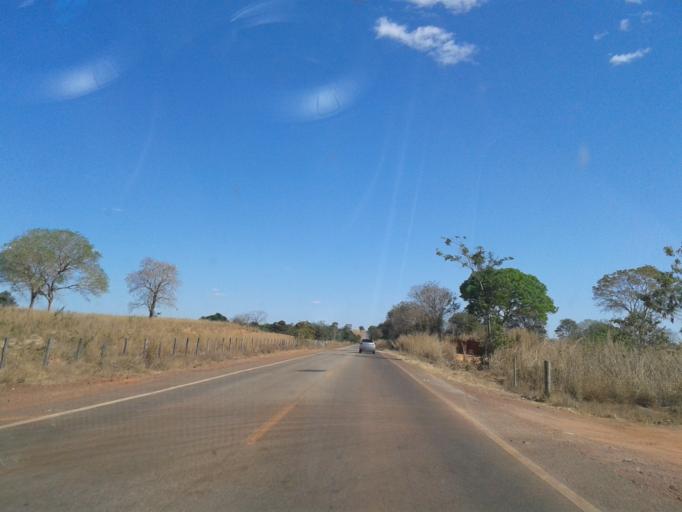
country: BR
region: Goias
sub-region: Crixas
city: Crixas
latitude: -14.1299
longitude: -50.3512
